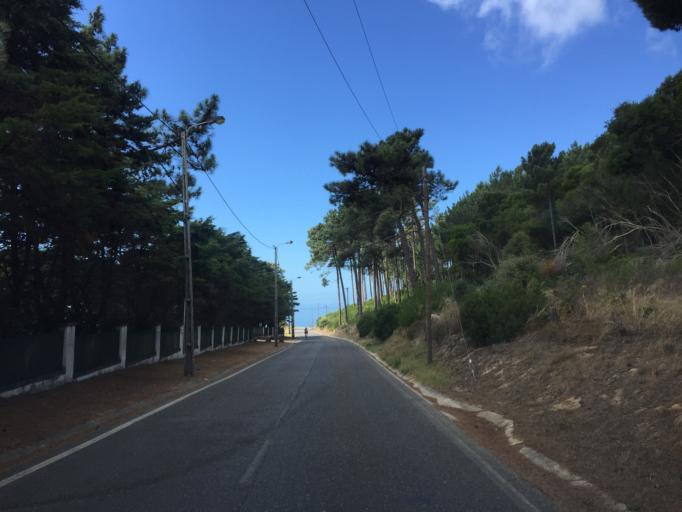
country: PT
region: Lisbon
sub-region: Cascais
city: Alcabideche
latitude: 38.7591
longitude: -9.4379
